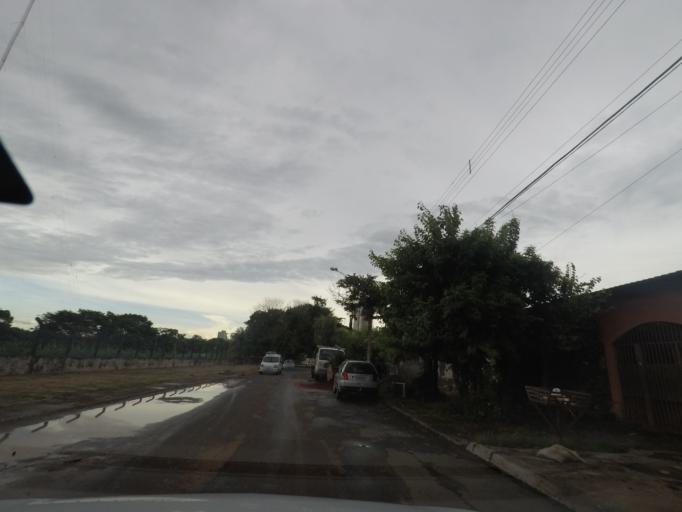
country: BR
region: Goias
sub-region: Goiania
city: Goiania
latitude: -16.7168
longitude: -49.2448
